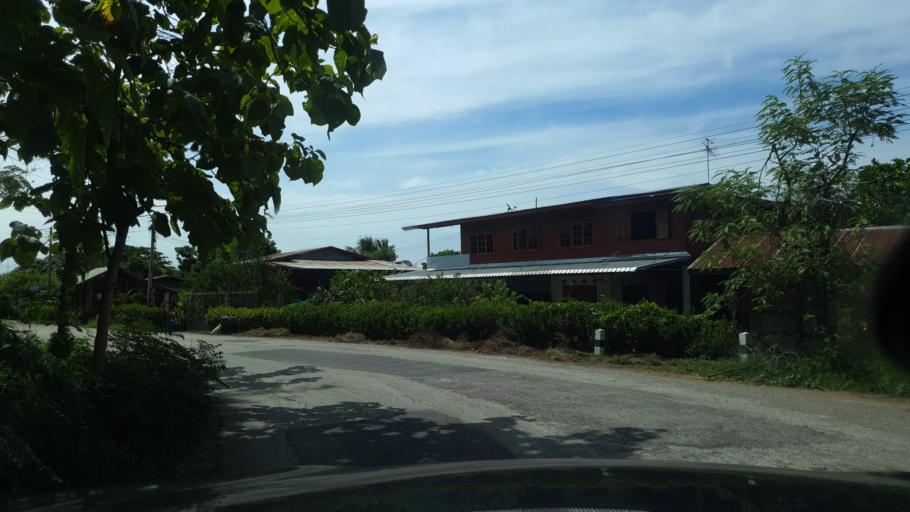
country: TH
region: Sukhothai
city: Si Samrong
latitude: 17.1986
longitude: 99.7230
